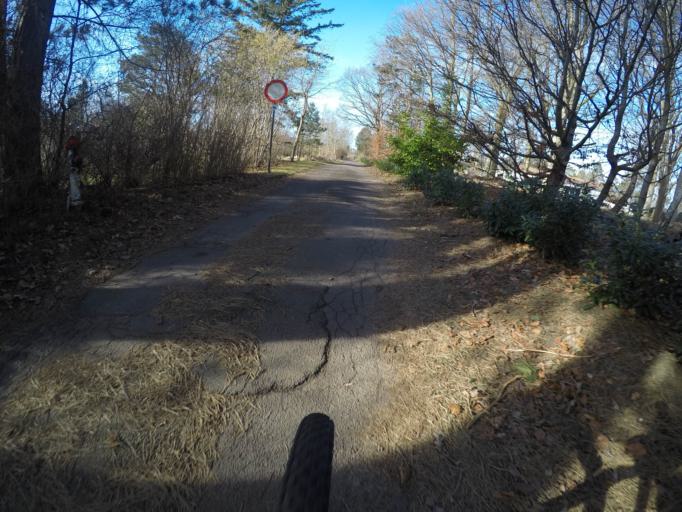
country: DK
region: Capital Region
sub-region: Halsnaes Kommune
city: Liseleje
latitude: 55.9962
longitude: 11.9315
